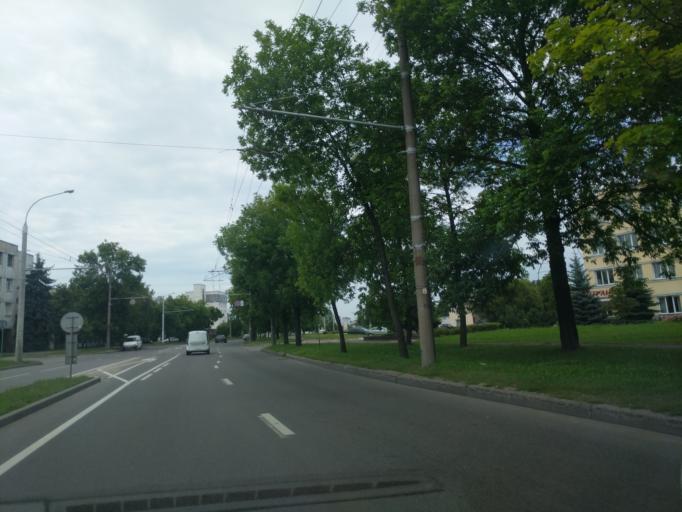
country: BY
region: Minsk
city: Novoye Medvezhino
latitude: 53.8828
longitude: 27.4827
